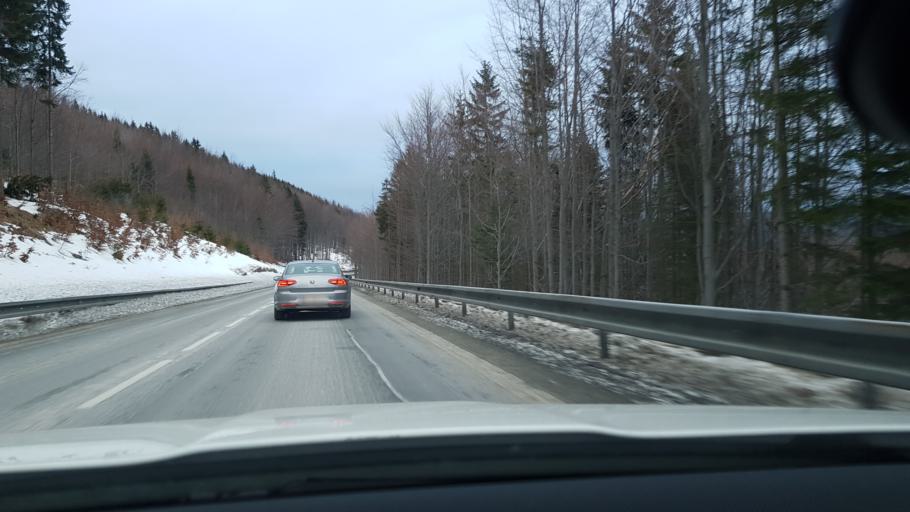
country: CZ
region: Olomoucky
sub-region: Okres Jesenik
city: Jesenik
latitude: 50.1411
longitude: 17.1652
